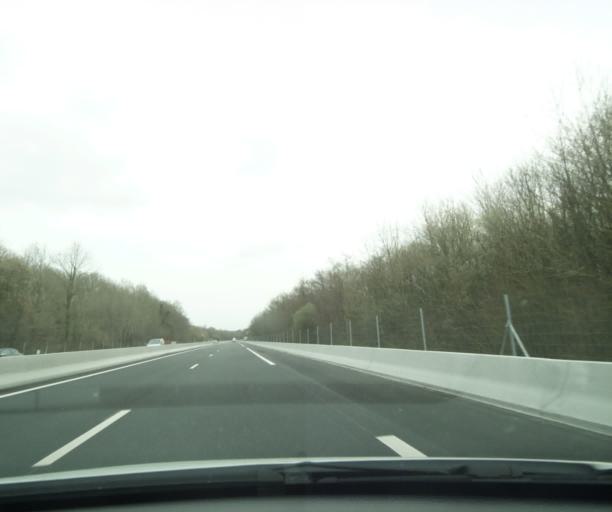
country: FR
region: Aquitaine
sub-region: Departement des Pyrenees-Atlantiques
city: Mouguerre
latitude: 43.4558
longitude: -1.4110
